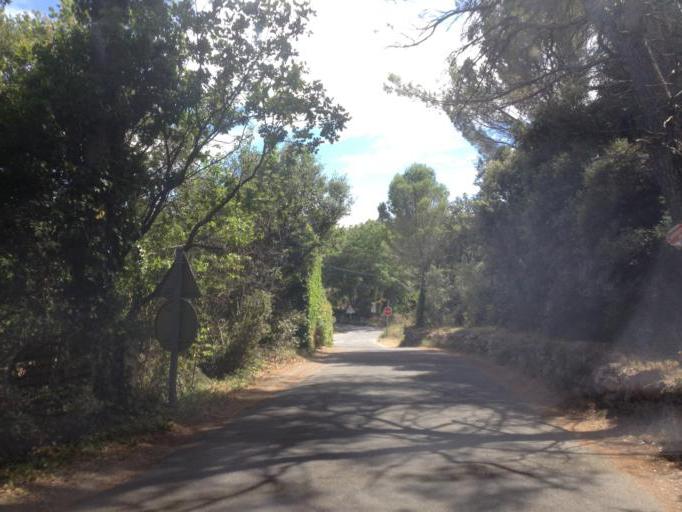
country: FR
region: Provence-Alpes-Cote d'Azur
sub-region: Departement du Vaucluse
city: Malaucene
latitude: 44.1495
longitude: 5.1019
